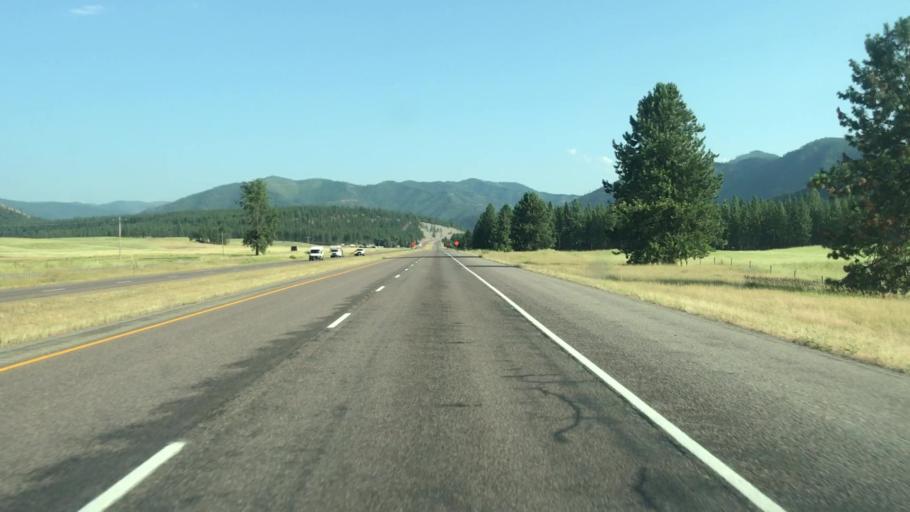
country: US
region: Montana
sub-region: Mineral County
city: Superior
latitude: 47.0396
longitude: -114.7487
